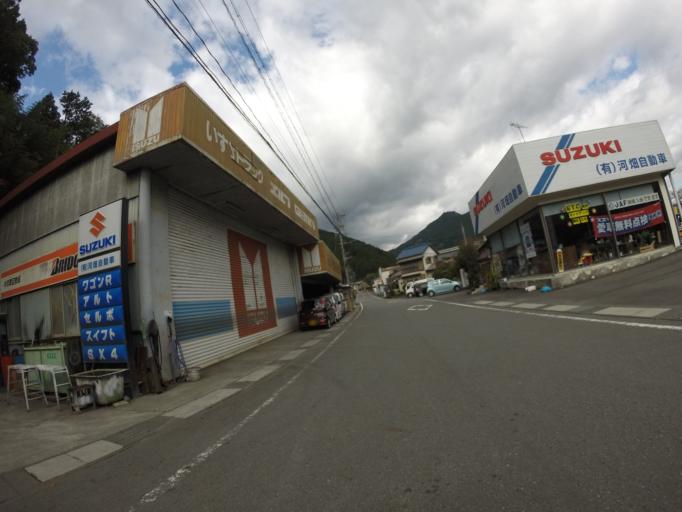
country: JP
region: Shizuoka
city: Kanaya
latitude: 35.0371
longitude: 138.0816
